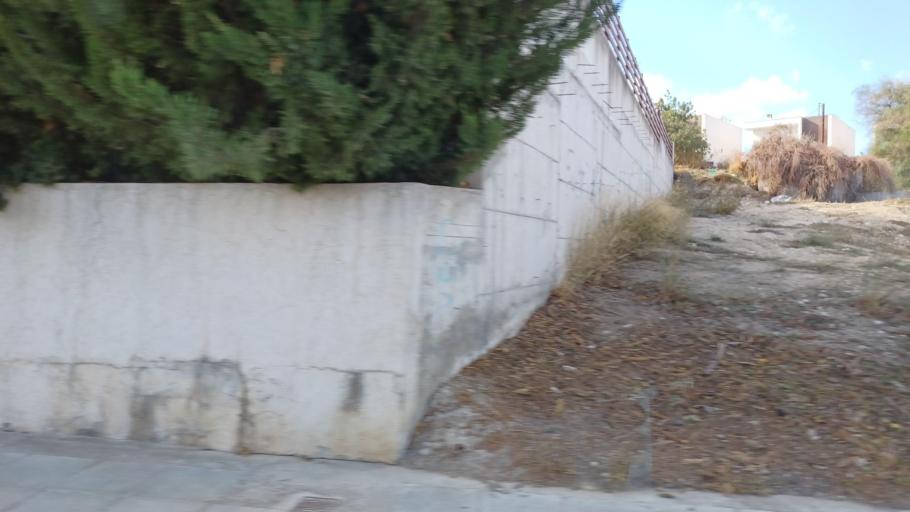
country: CY
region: Limassol
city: Pano Polemidia
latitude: 34.7426
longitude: 33.0043
